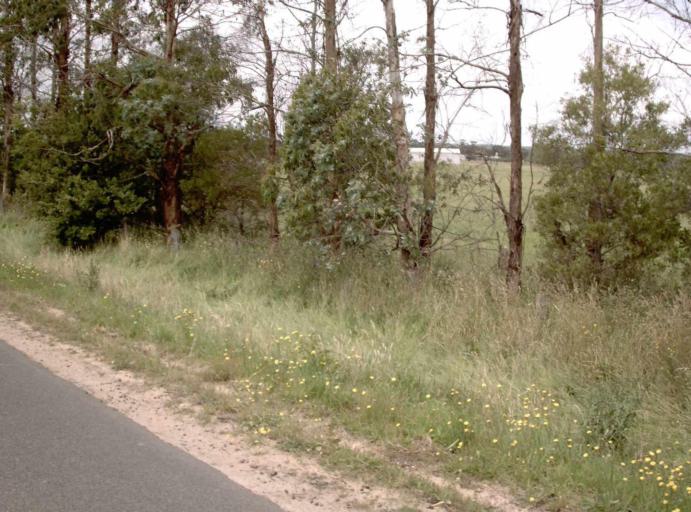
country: AU
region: Victoria
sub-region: Latrobe
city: Traralgon
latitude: -38.4993
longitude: 146.6742
